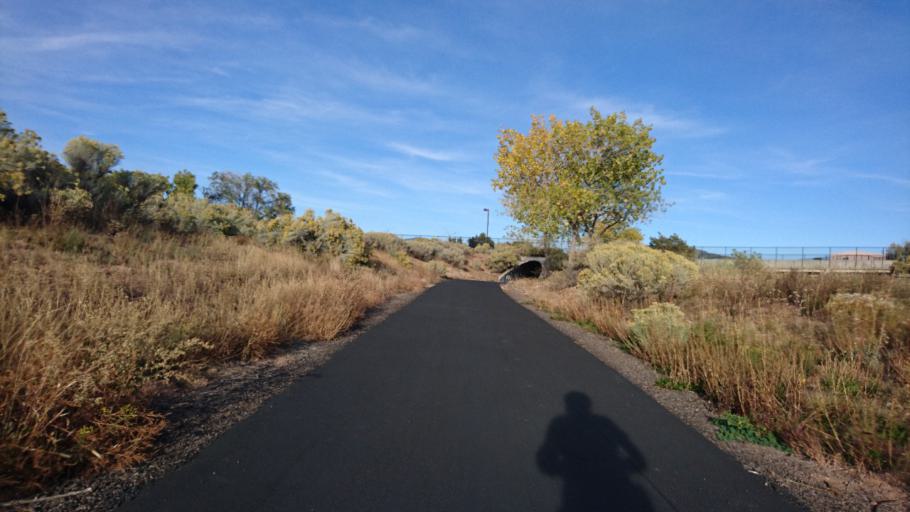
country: US
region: New Mexico
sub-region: Santa Fe County
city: Santa Fe
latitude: 35.6474
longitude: -105.9696
